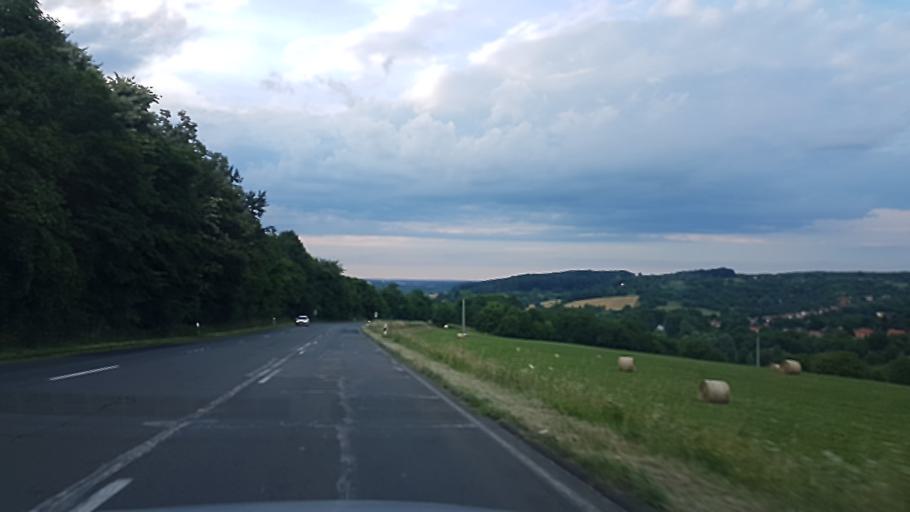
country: HU
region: Somogy
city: Kaposvar
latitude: 46.2748
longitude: 17.8221
